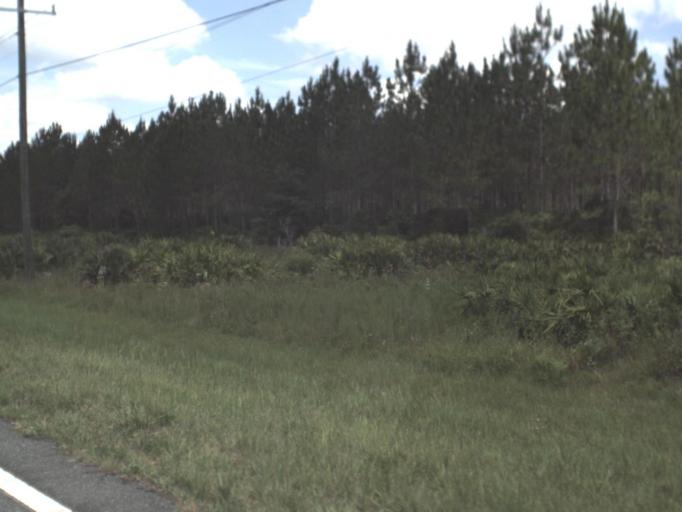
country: US
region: Florida
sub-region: Levy County
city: Chiefland
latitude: 29.2428
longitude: -82.9236
